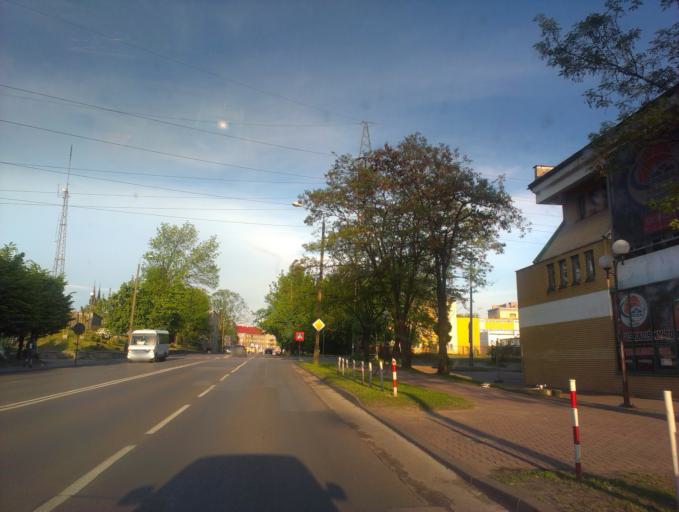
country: PL
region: Masovian Voivodeship
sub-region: Radom
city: Radom
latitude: 51.3974
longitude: 21.1477
